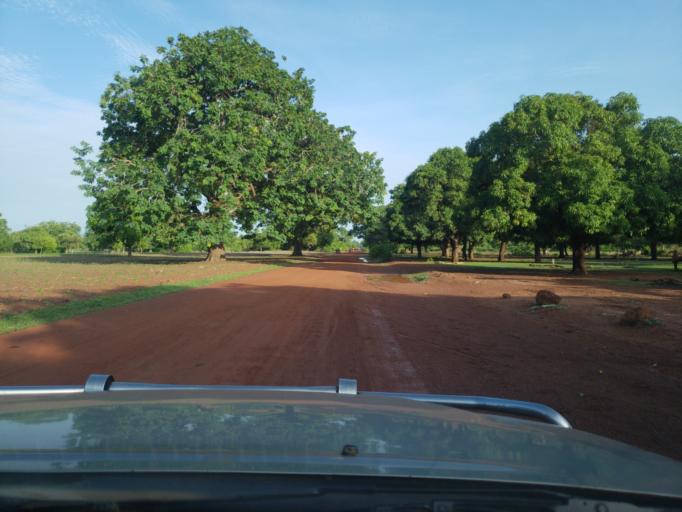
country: ML
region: Sikasso
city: Koutiala
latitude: 12.4214
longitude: -5.5844
